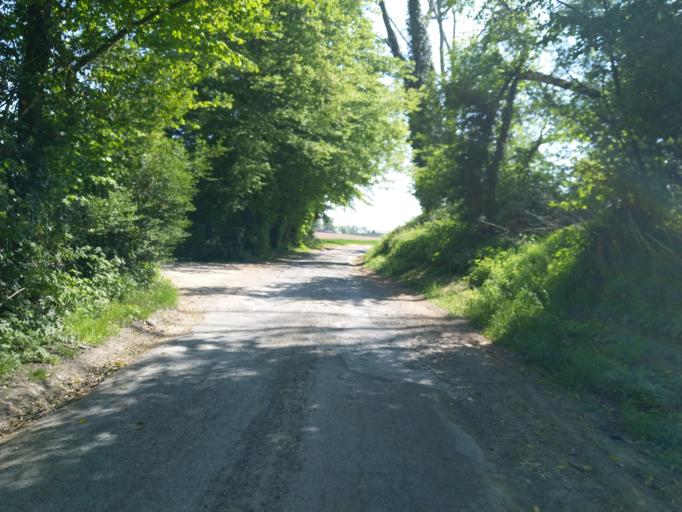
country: BE
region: Wallonia
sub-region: Province du Brabant Wallon
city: Rebecq-Rognon
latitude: 50.6164
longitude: 4.1078
